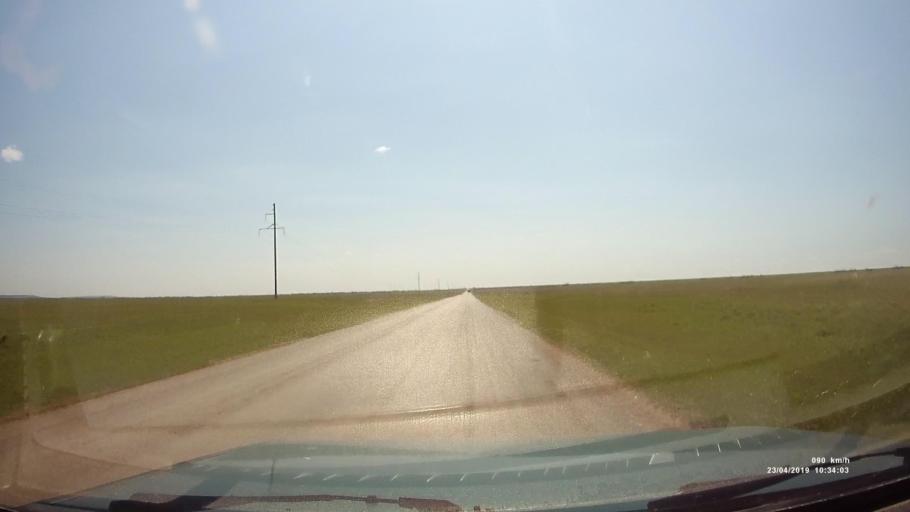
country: RU
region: Kalmykiya
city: Yashalta
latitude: 46.5677
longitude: 42.6053
